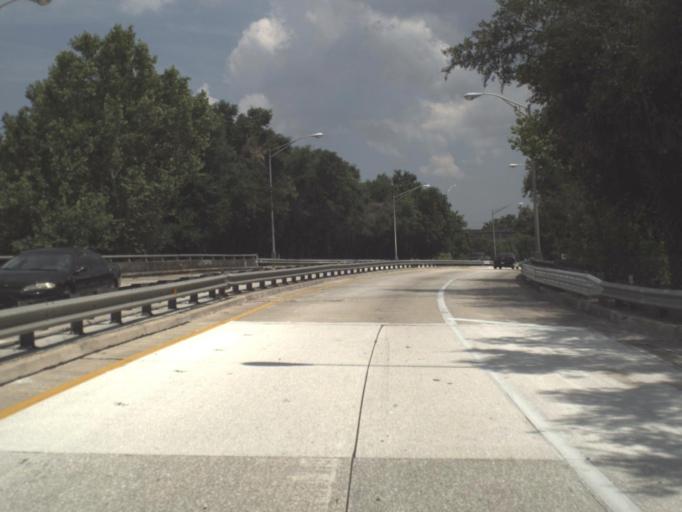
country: US
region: Florida
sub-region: Duval County
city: Jacksonville
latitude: 30.3292
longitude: -81.6349
